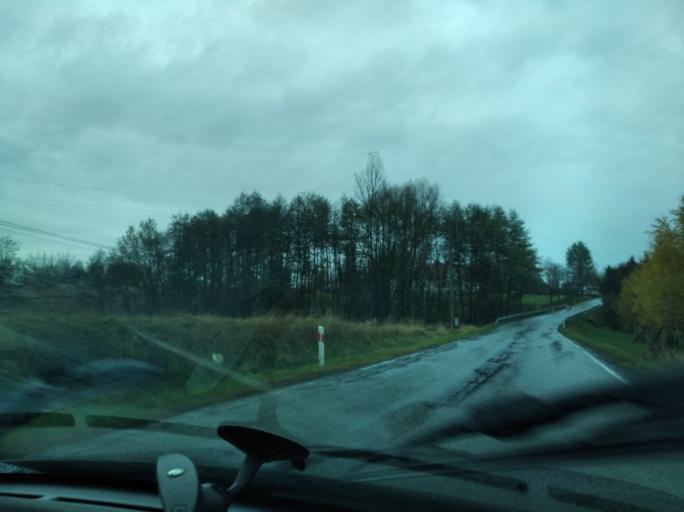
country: PL
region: Subcarpathian Voivodeship
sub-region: Powiat lancucki
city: Handzlowka
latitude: 49.9949
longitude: 22.1936
